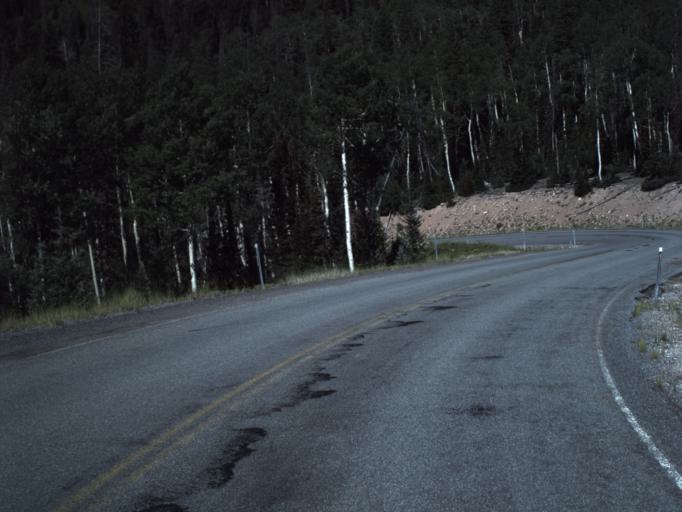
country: US
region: Utah
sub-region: Piute County
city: Junction
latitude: 38.3170
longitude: -112.3680
